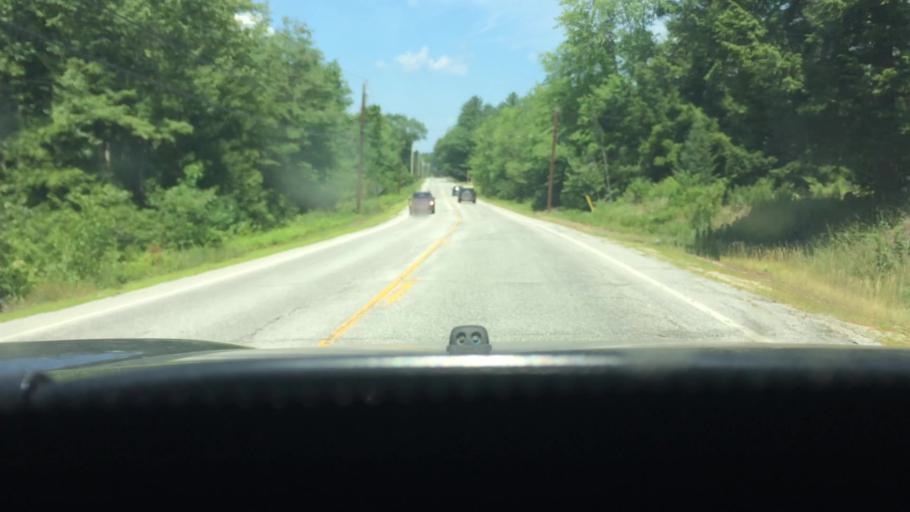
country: US
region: Maine
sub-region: Androscoggin County
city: Mechanic Falls
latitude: 44.1145
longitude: -70.4241
